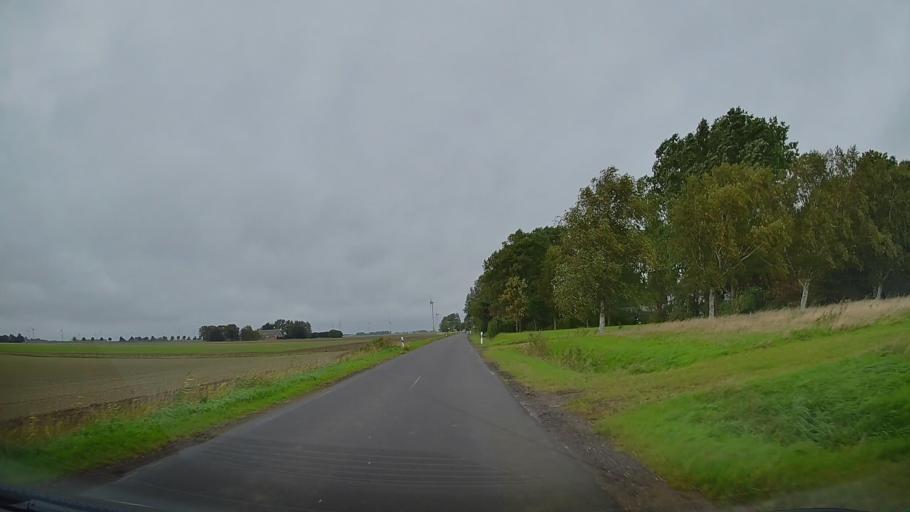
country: DE
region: Schleswig-Holstein
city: Marnerdeich
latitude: 53.9261
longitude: 8.9845
